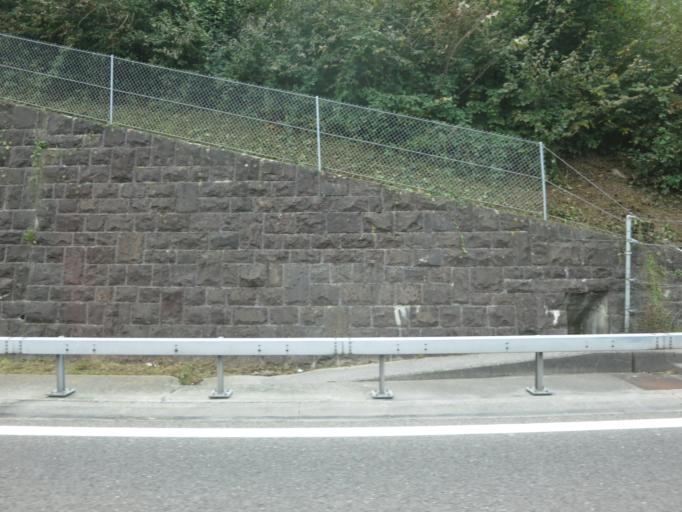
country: CH
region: Saint Gallen
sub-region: Wahlkreis See-Gaster
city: Amden
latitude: 47.1160
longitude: 9.1810
